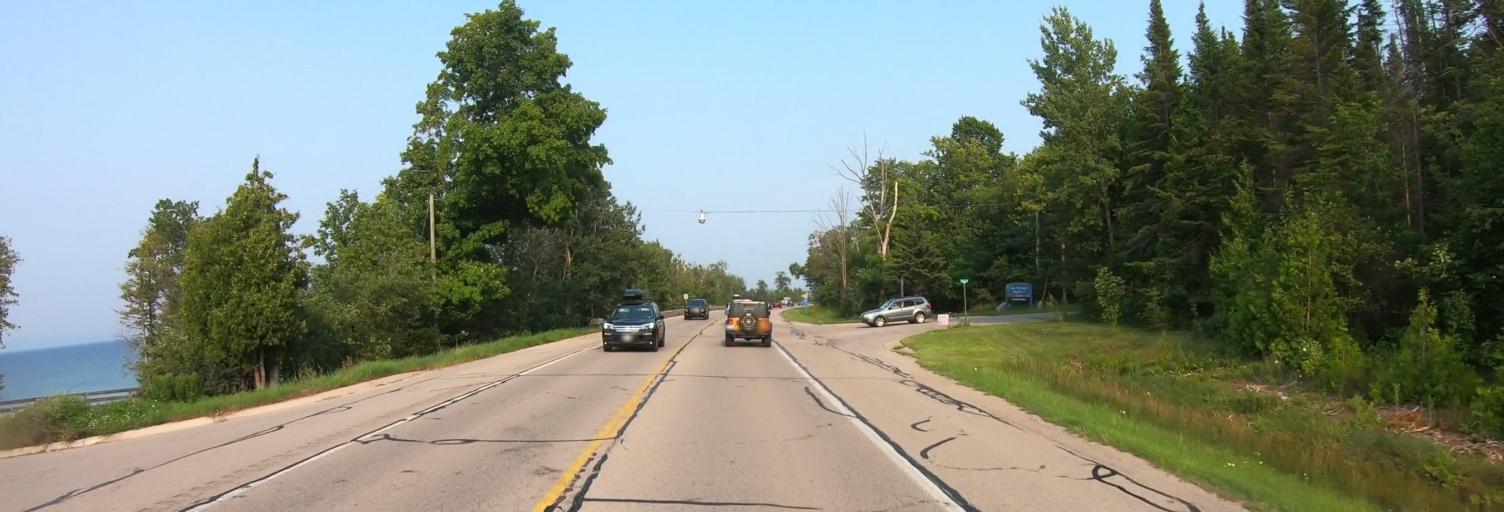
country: US
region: Michigan
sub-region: Charlevoix County
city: Charlevoix
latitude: 45.3690
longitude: -85.1335
